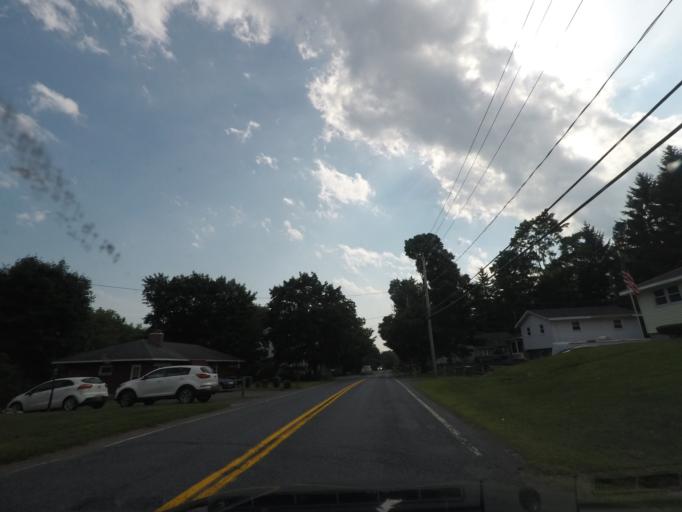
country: US
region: New York
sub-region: Albany County
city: Green Island
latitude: 42.7493
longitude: -73.6578
